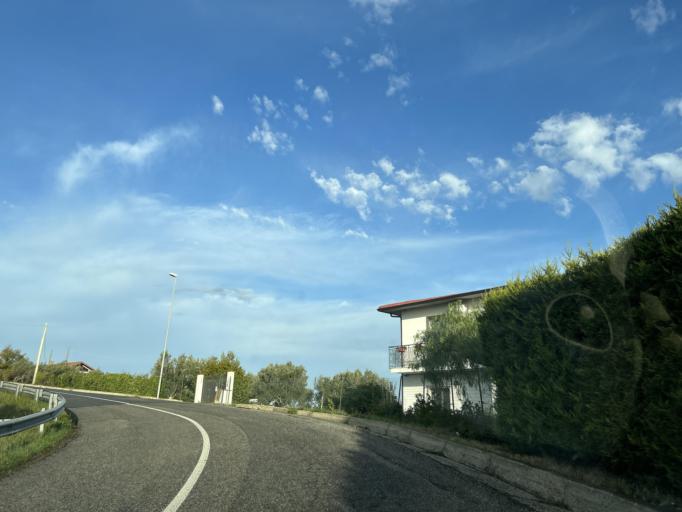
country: IT
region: Calabria
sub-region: Provincia di Catanzaro
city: Staletti
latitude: 38.7674
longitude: 16.5254
